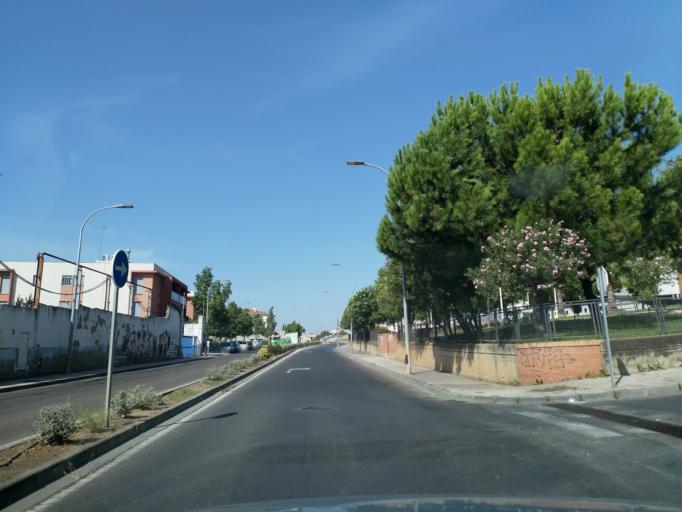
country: ES
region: Extremadura
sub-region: Provincia de Badajoz
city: Merida
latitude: 38.9247
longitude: -6.3420
